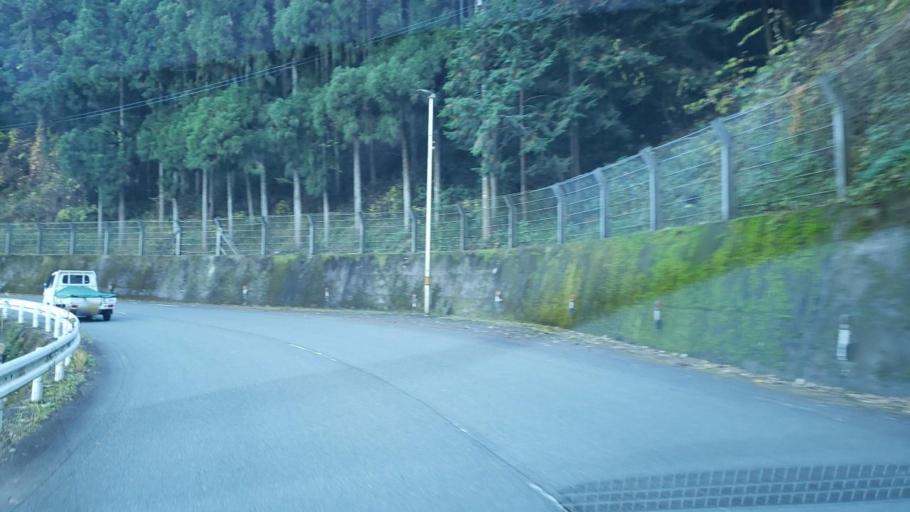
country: JP
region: Tokushima
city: Wakimachi
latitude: 34.0211
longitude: 134.0360
